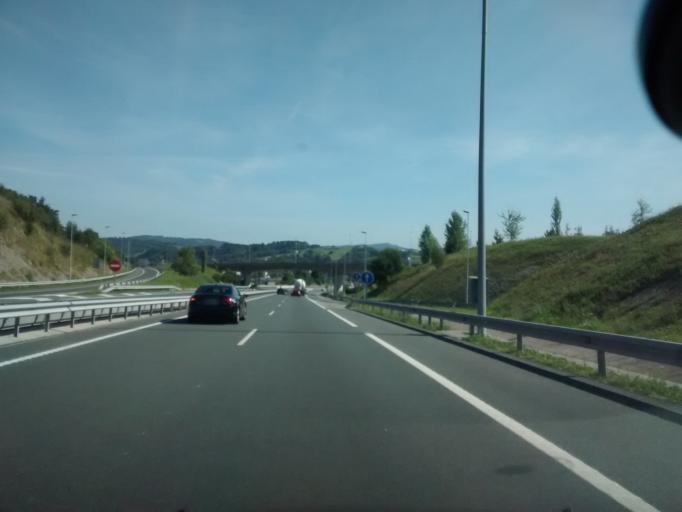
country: ES
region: Basque Country
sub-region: Provincia de Guipuzcoa
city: Astigarraga
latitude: 43.2803
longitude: -1.9612
